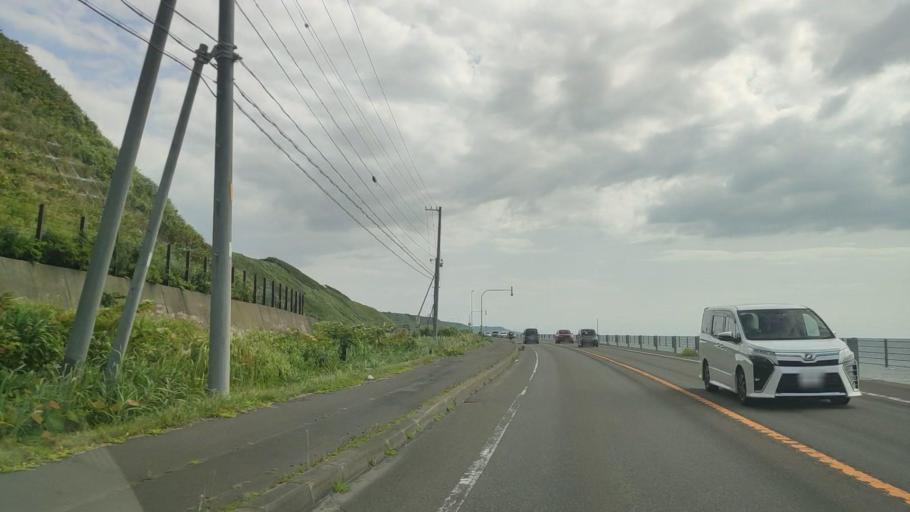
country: JP
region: Hokkaido
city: Rumoi
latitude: 44.2136
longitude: 141.6565
